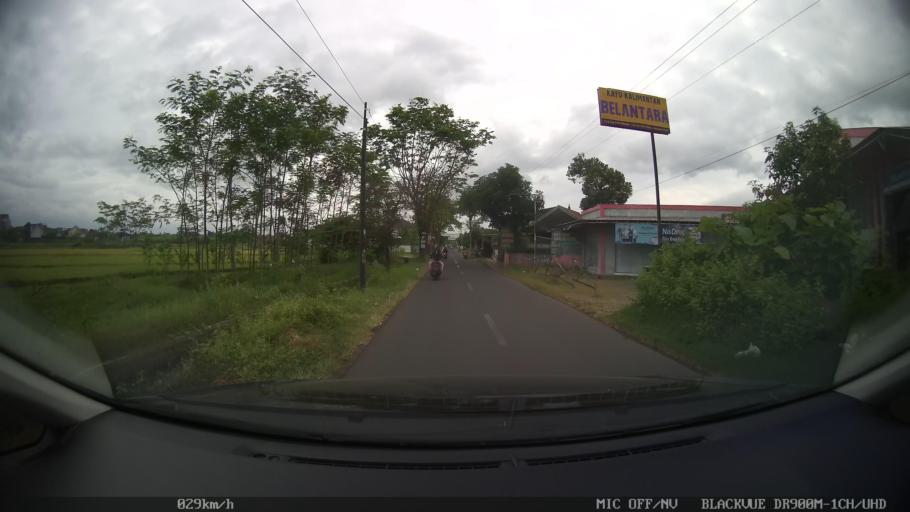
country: ID
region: Daerah Istimewa Yogyakarta
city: Sewon
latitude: -7.8381
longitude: 110.4128
